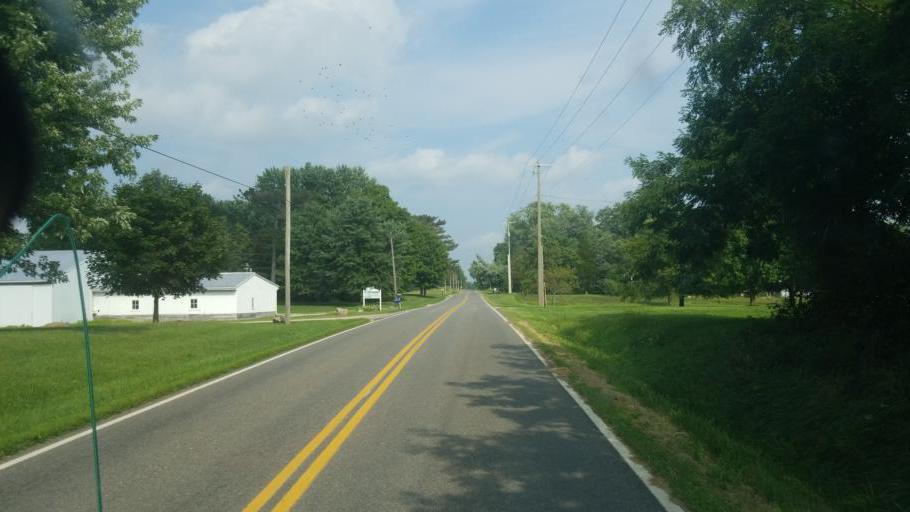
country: US
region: Ohio
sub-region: Medina County
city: Medina
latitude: 41.1423
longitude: -81.9207
